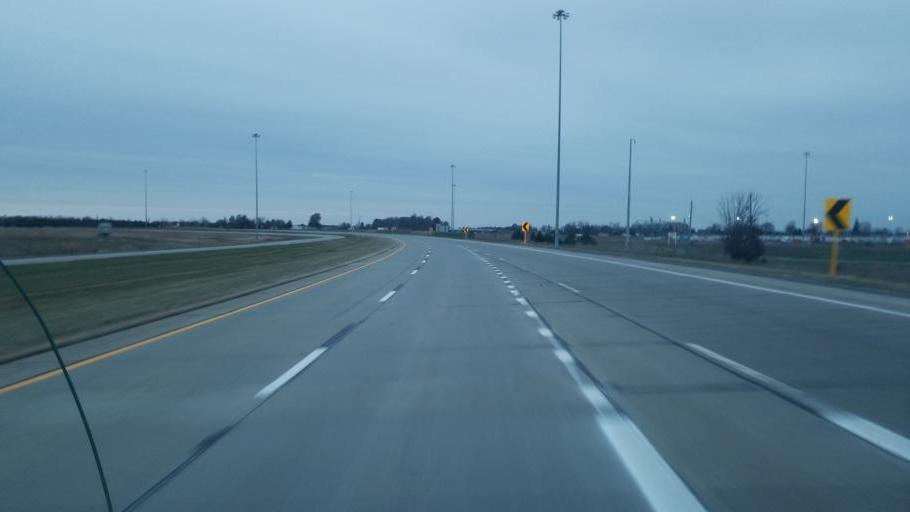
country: US
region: Ohio
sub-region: Allen County
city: Bluffton
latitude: 40.8294
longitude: -83.9600
